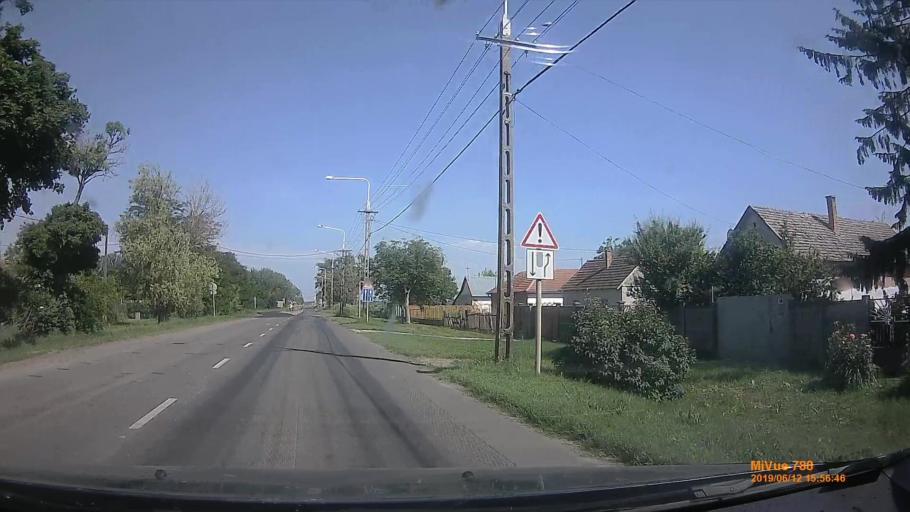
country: HU
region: Csongrad
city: Apatfalva
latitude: 46.1685
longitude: 20.6227
